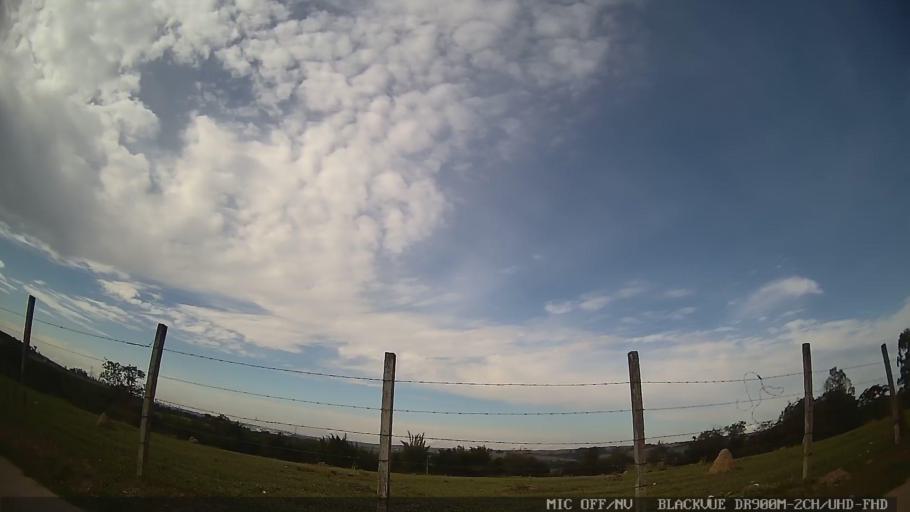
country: BR
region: Sao Paulo
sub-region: Salto
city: Salto
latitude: -23.1750
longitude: -47.2661
